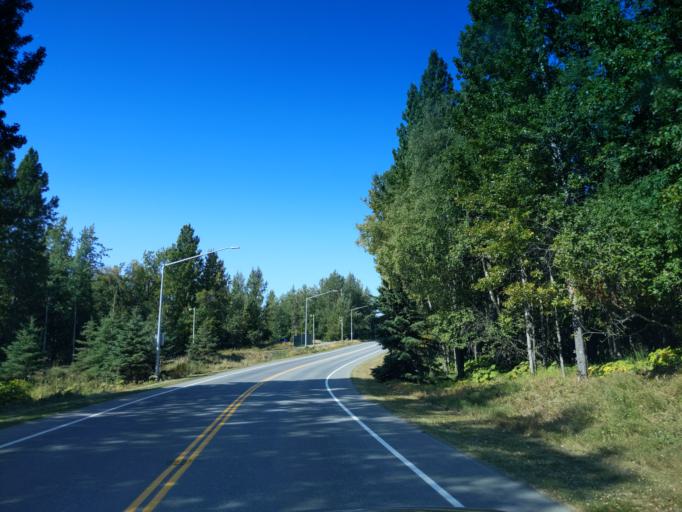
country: US
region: Alaska
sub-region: Anchorage Municipality
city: Anchorage
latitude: 61.1542
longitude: -150.0322
